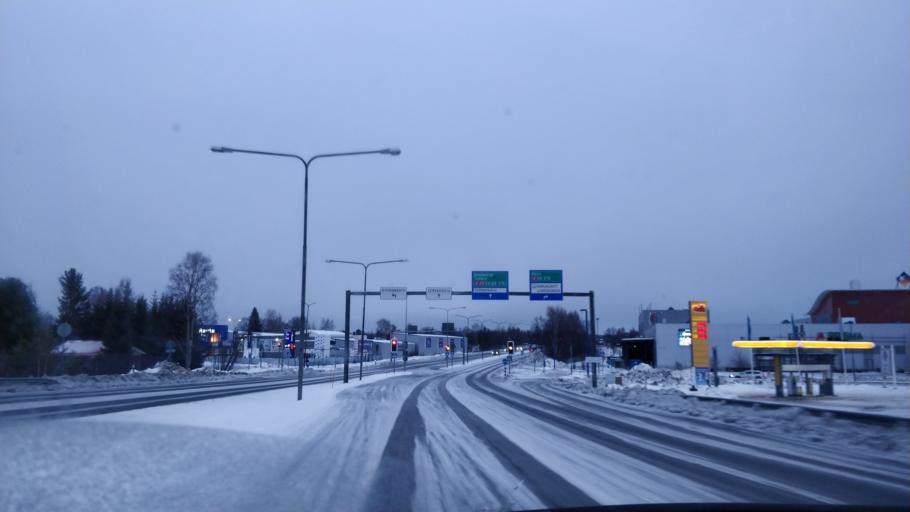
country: FI
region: Lapland
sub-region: Kemi-Tornio
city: Kemi
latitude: 65.7423
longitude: 24.5740
